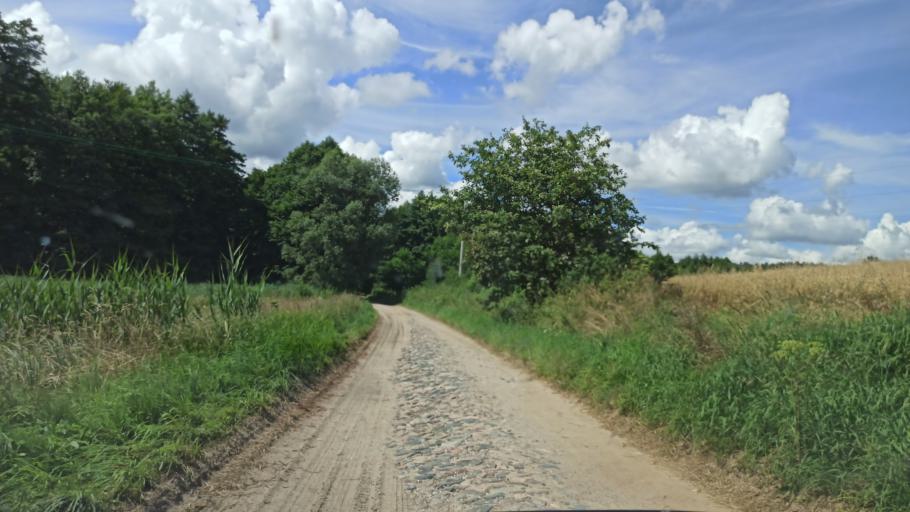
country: PL
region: Warmian-Masurian Voivodeship
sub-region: Powiat ostrodzki
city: Morag
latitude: 53.8667
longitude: 20.0562
